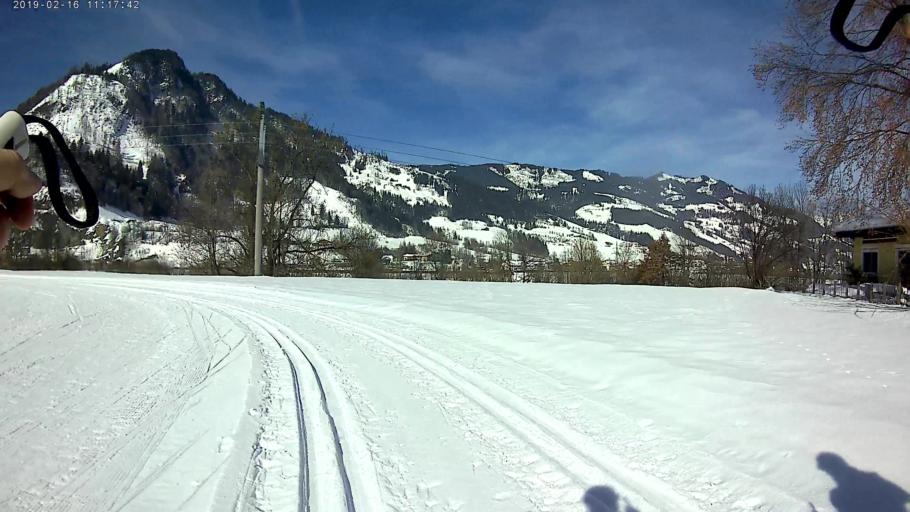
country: AT
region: Salzburg
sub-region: Politischer Bezirk Sankt Johann im Pongau
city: Sankt Johann im Pongau
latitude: 47.3298
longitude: 13.1921
